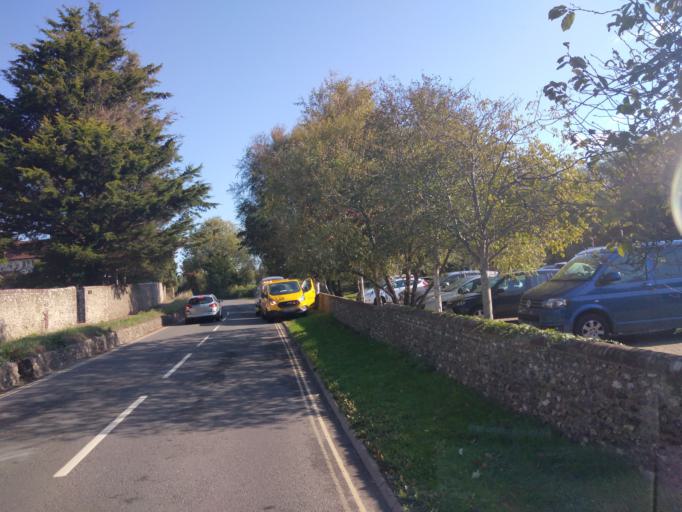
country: GB
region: England
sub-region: East Sussex
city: Seaford
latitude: 50.8093
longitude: 0.1572
